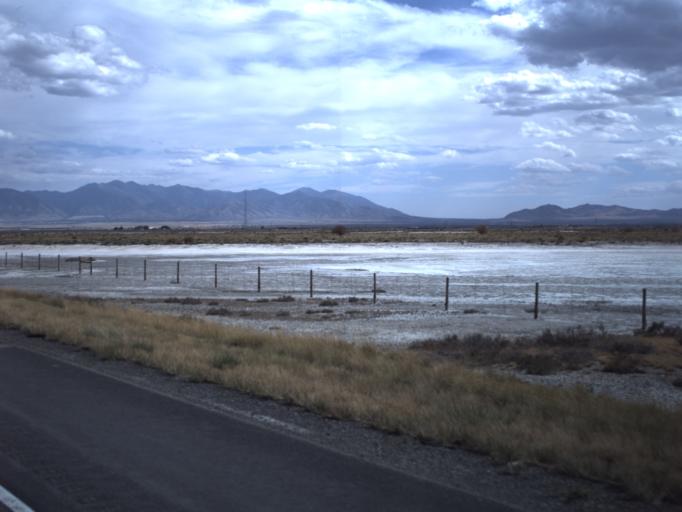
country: US
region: Utah
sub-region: Tooele County
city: Grantsville
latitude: 40.6928
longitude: -112.4684
